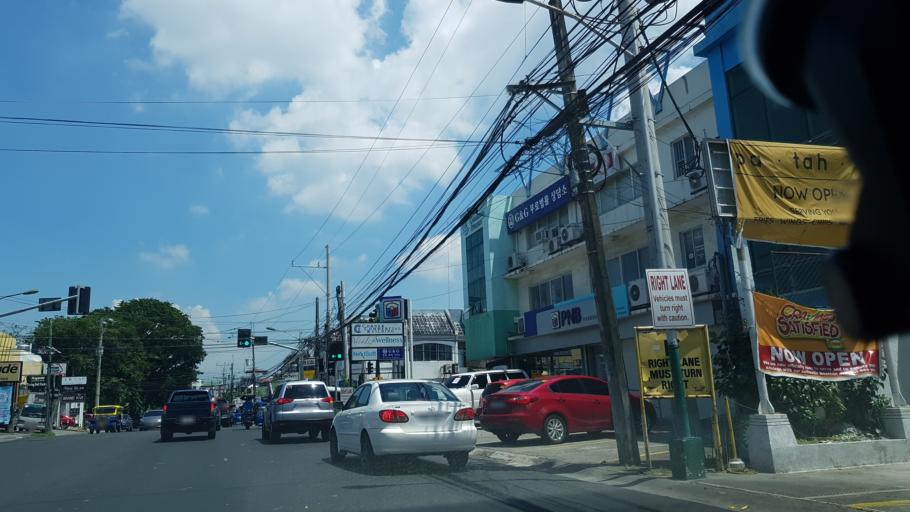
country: PH
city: Sambayanihan People's Village
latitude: 14.4449
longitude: 121.0246
